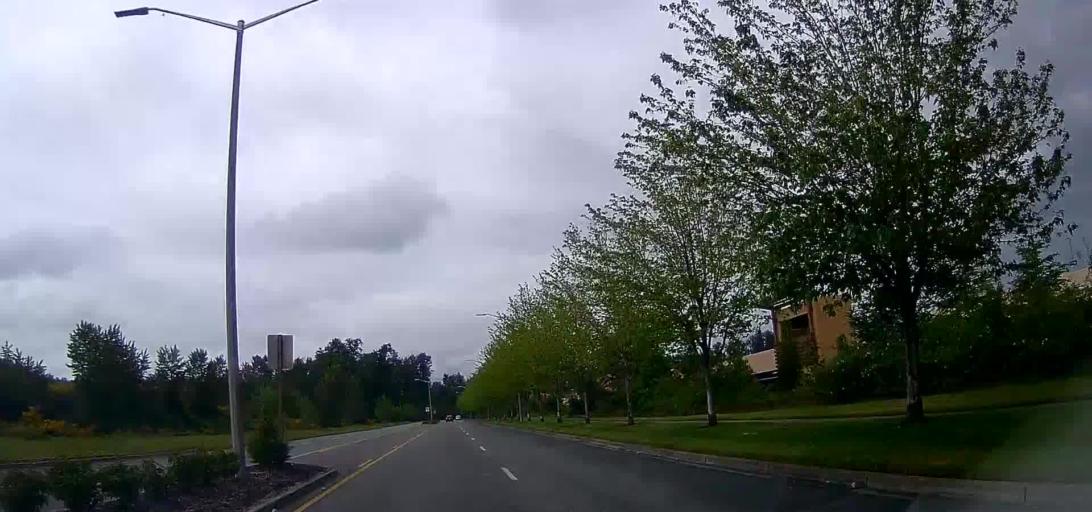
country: US
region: Washington
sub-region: Snohomish County
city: Marysville
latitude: 48.0915
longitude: -122.1908
